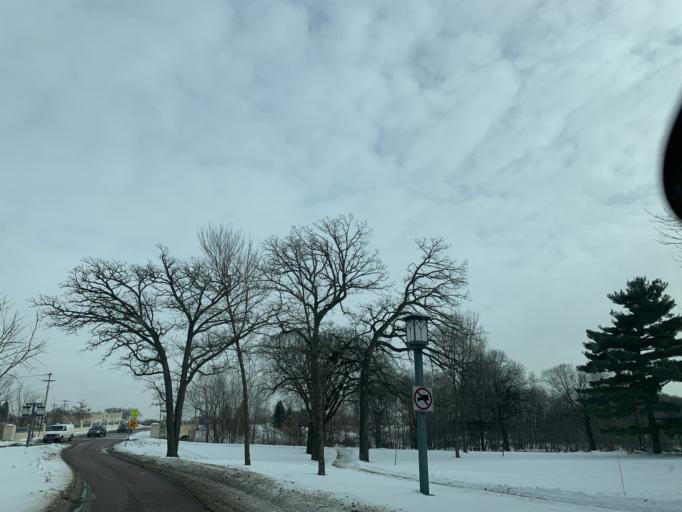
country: US
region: Minnesota
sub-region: Hennepin County
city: Richfield
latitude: 44.9161
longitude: -93.2176
